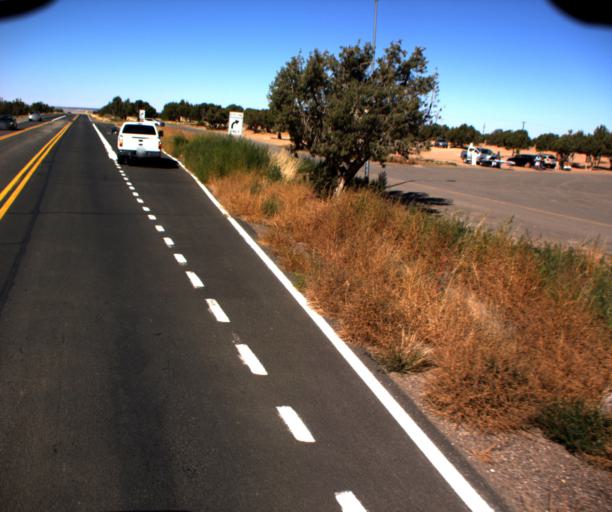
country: US
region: Arizona
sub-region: Navajo County
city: First Mesa
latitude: 35.8436
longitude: -110.5296
